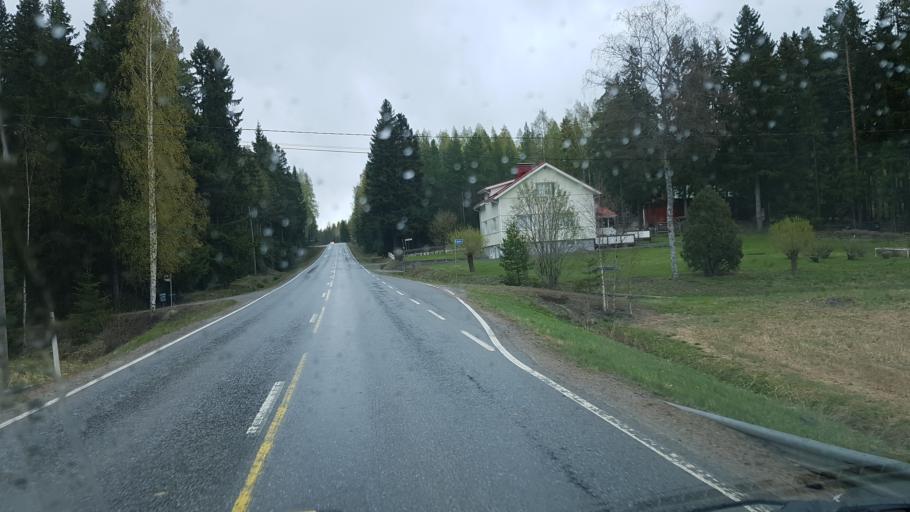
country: FI
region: Pirkanmaa
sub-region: Tampere
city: Pirkkala
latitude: 61.3935
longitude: 23.6234
